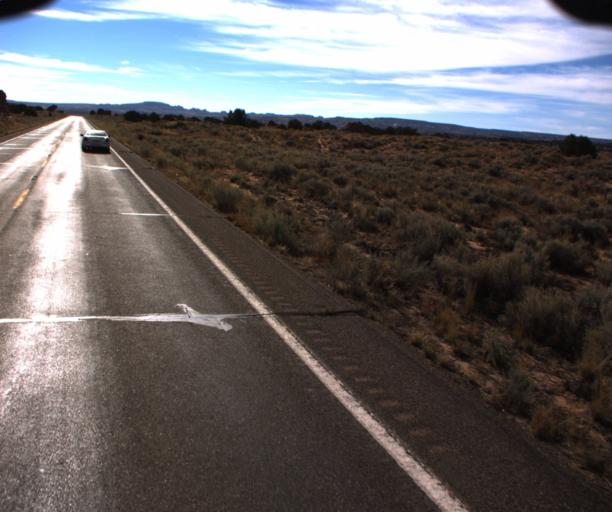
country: US
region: Arizona
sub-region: Coconino County
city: Kaibito
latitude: 36.6338
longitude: -111.2107
